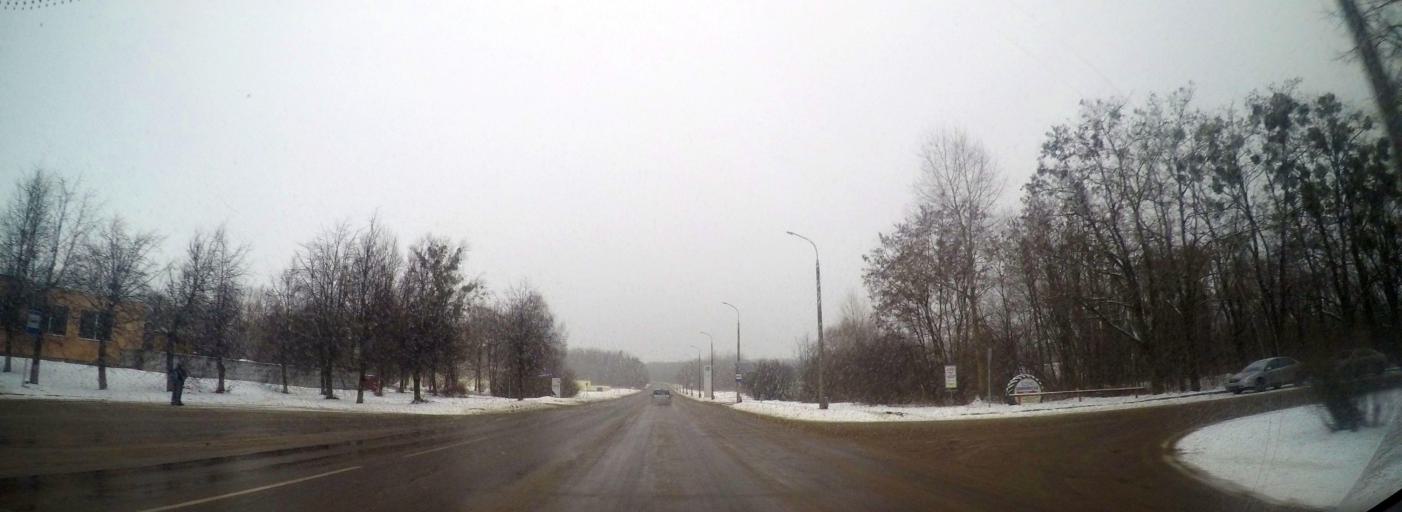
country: BY
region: Grodnenskaya
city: Hrodna
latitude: 53.6853
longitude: 23.8799
